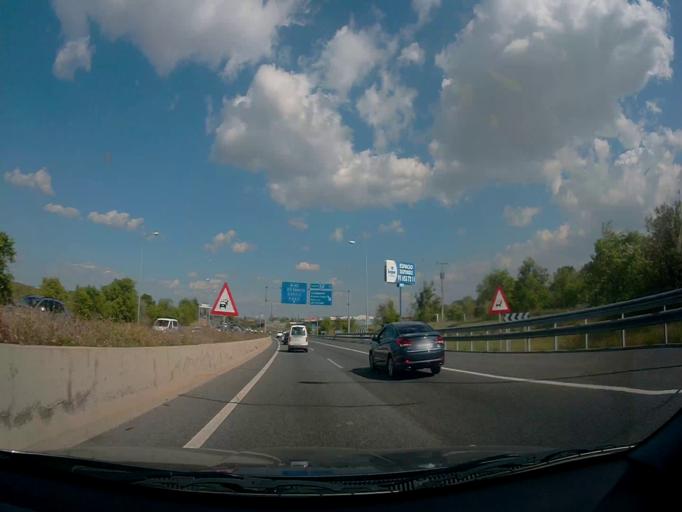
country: ES
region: Madrid
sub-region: Provincia de Madrid
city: Alcorcon
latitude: 40.3613
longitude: -3.7935
